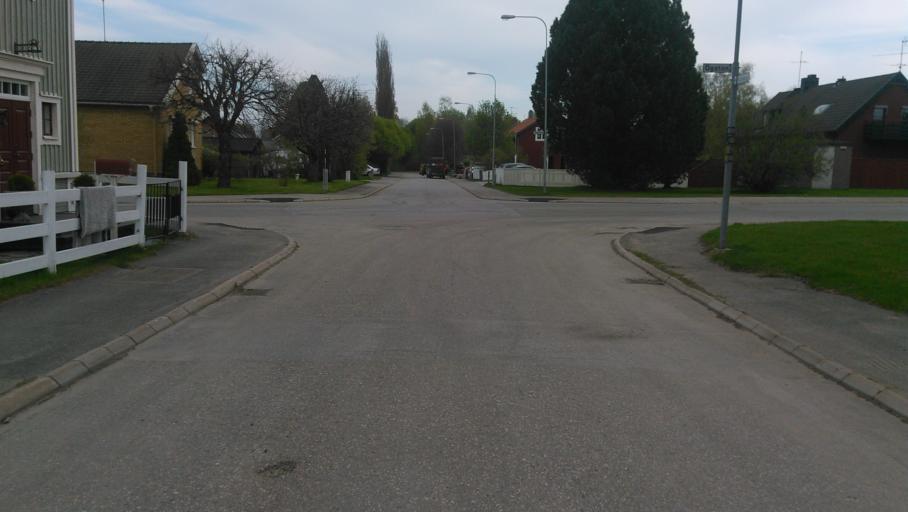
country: SE
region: Vaesterbotten
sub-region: Umea Kommun
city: Umea
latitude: 63.8110
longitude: 20.2697
